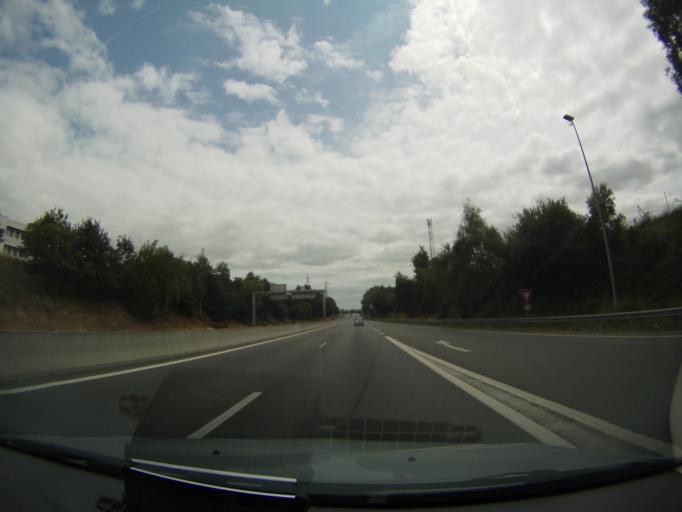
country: FR
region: Pays de la Loire
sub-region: Departement de la Loire-Atlantique
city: Sainte-Luce-sur-Loire
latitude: 47.2519
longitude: -1.5125
